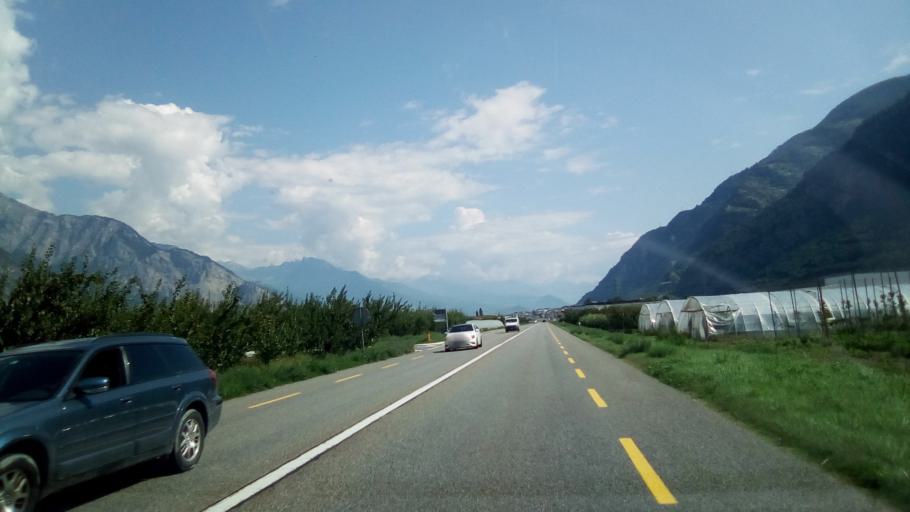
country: CH
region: Valais
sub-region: Martigny District
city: Saxon
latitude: 46.1582
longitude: 7.1934
